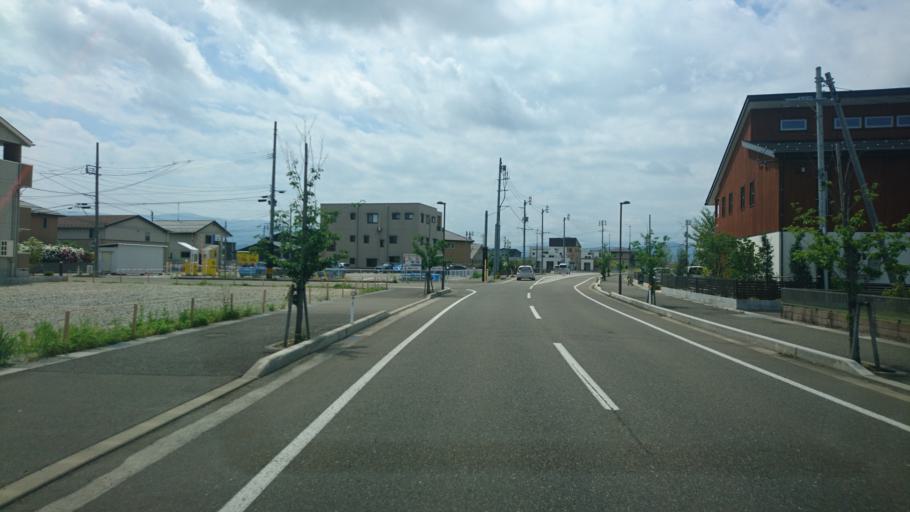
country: JP
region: Niigata
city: Joetsu
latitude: 37.0799
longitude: 138.2468
